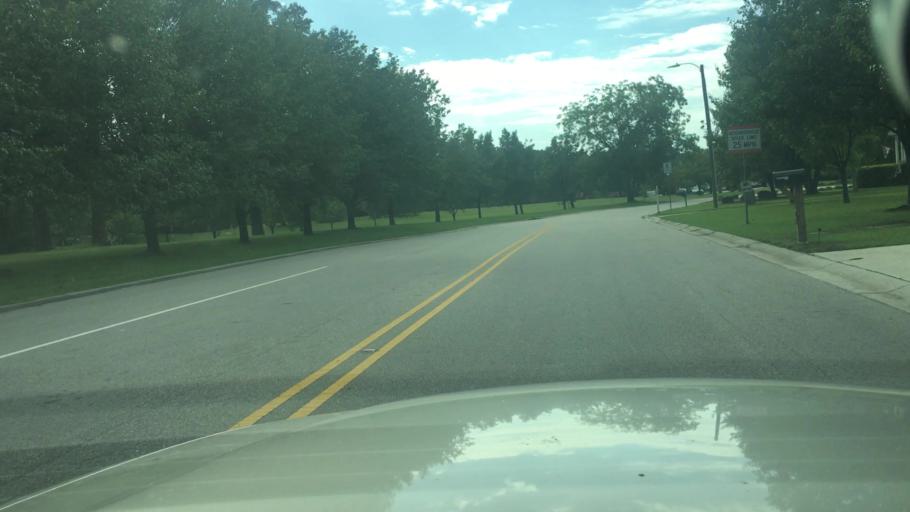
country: US
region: North Carolina
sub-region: Cumberland County
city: Eastover
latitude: 35.1600
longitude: -78.8686
